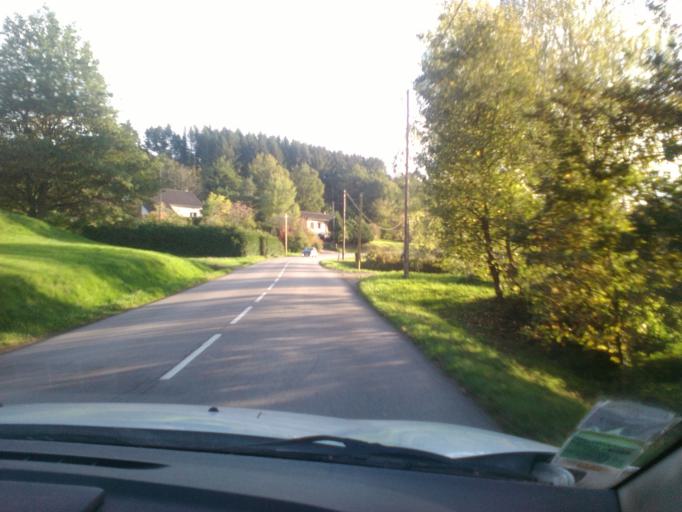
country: FR
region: Lorraine
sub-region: Departement des Vosges
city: Taintrux
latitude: 48.2471
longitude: 6.8979
